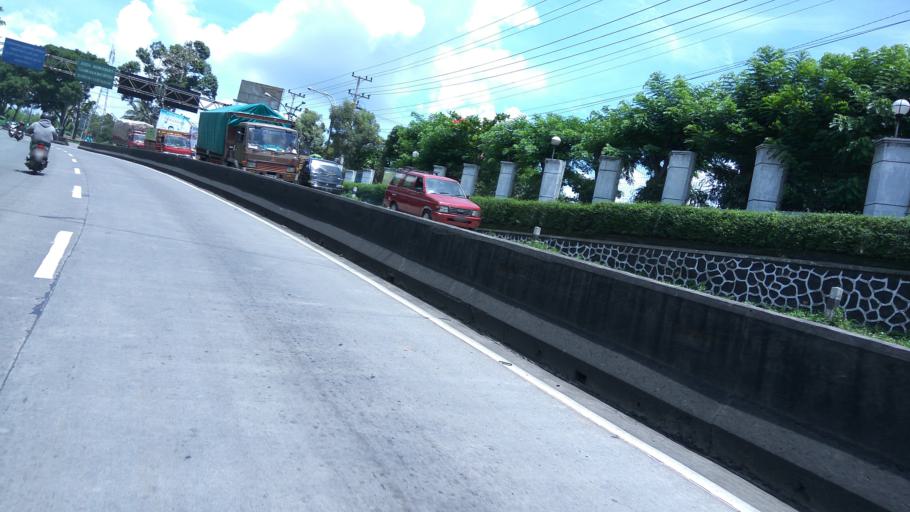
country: ID
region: Central Java
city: Ambarawa
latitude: -7.2412
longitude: 110.4351
